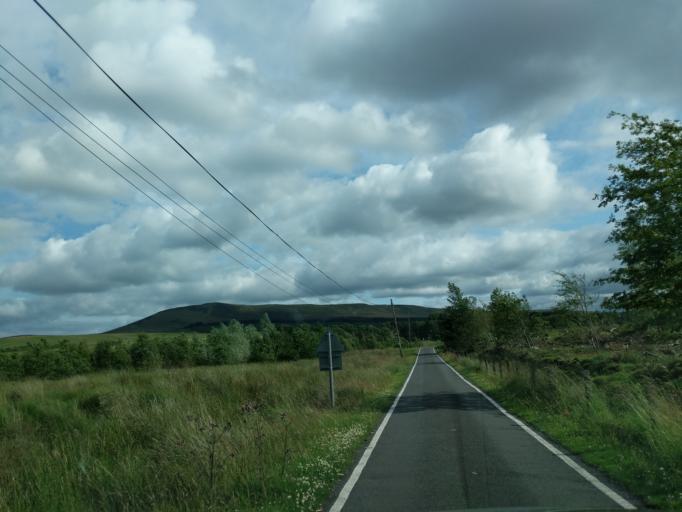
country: GB
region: Scotland
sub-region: West Lothian
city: East Calder
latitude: 55.8330
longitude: -3.4571
